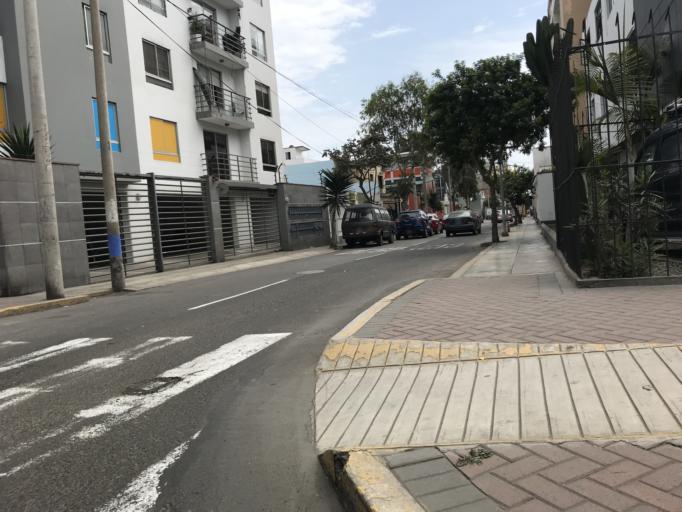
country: PE
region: Lima
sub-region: Lima
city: San Isidro
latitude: -12.1140
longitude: -77.0437
